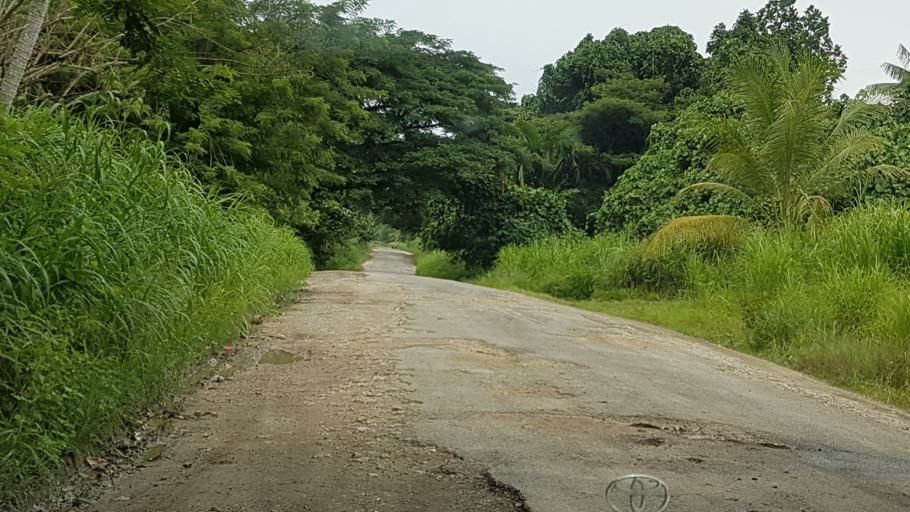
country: PG
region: Madang
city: Madang
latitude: -4.7147
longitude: 145.6325
